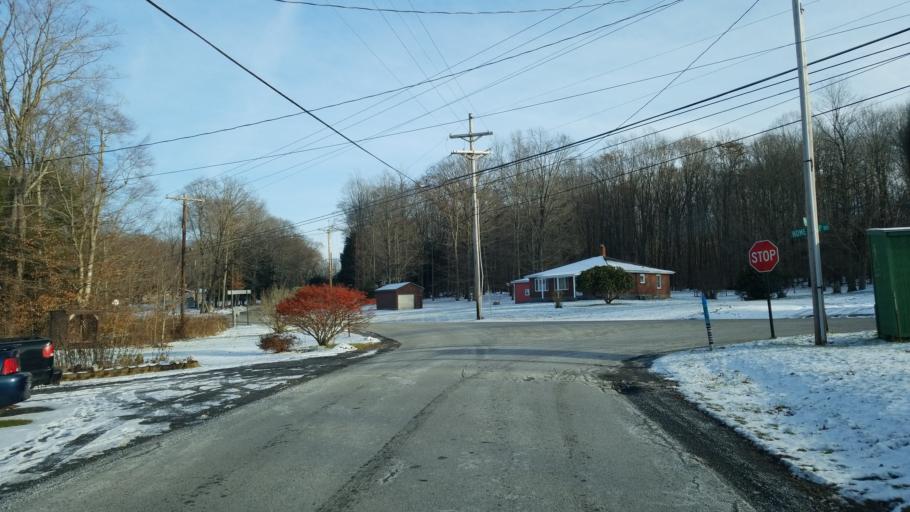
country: US
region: Pennsylvania
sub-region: Clearfield County
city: DuBois
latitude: 41.1093
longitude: -78.6968
